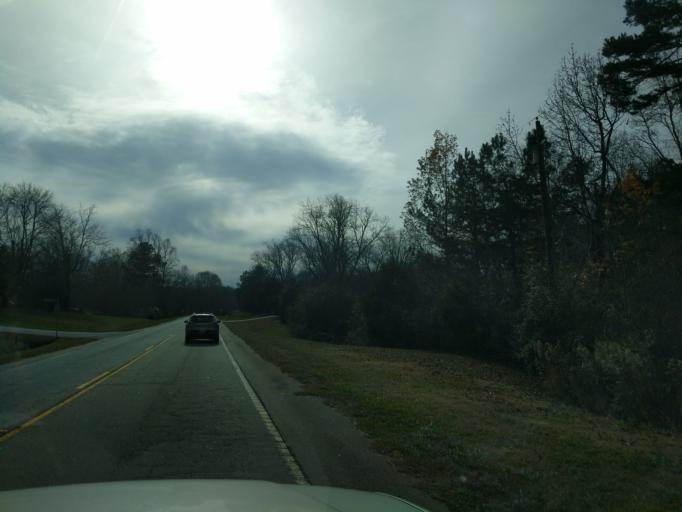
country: US
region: South Carolina
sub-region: Oconee County
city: Walhalla
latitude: 34.7733
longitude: -83.0292
